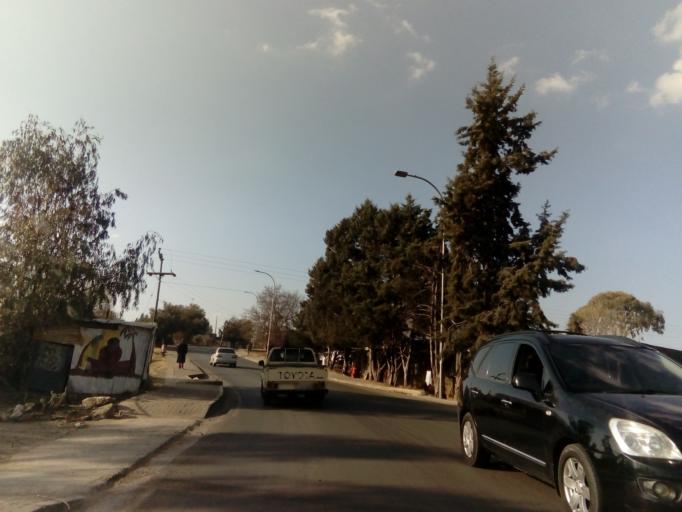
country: LS
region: Maseru
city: Maseru
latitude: -29.3081
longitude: 27.5308
